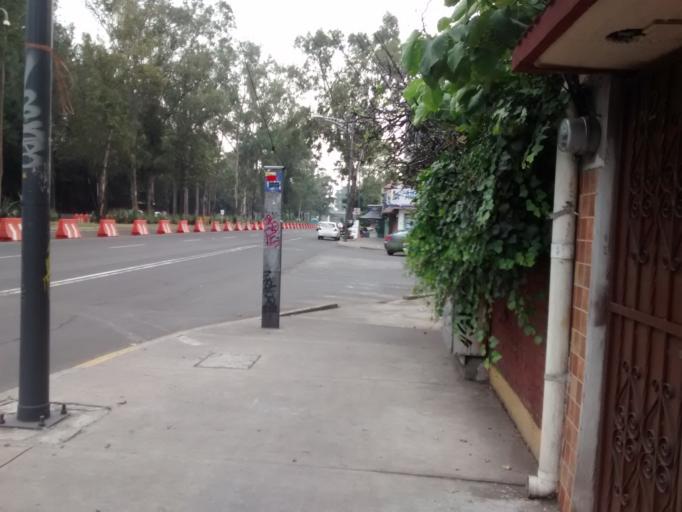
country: MX
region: Mexico City
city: Coyoacan
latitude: 19.3317
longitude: -99.1135
